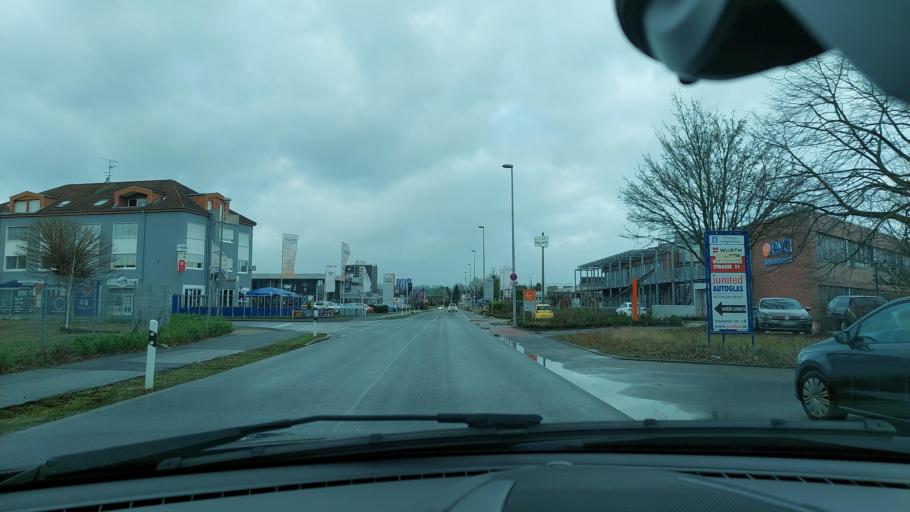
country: DE
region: North Rhine-Westphalia
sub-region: Regierungsbezirk Dusseldorf
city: Dormagen
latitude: 51.0928
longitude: 6.8202
